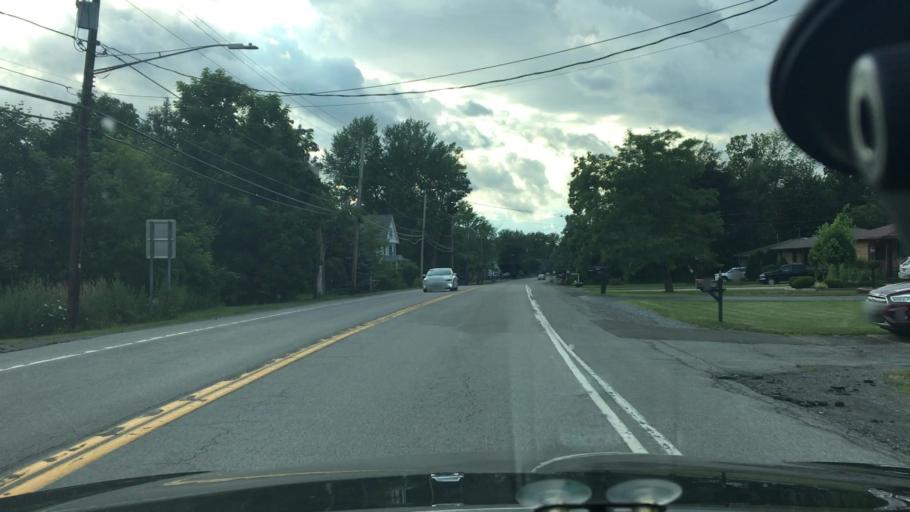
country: US
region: New York
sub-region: Erie County
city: Elma Center
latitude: 42.8280
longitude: -78.6996
